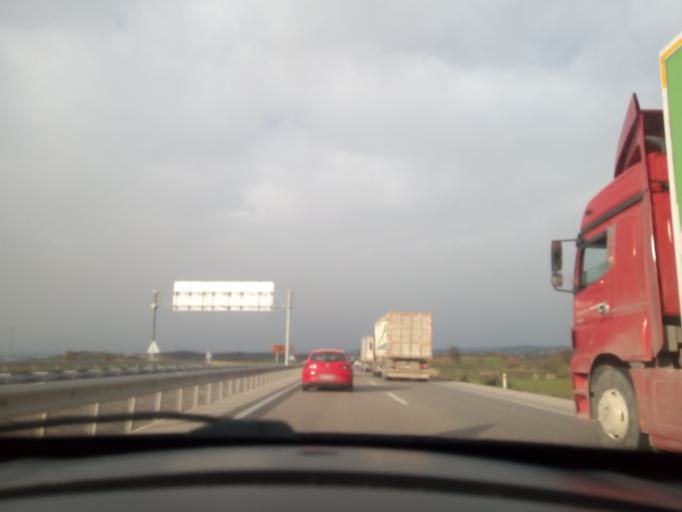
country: TR
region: Bursa
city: Mahmudiye
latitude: 40.2130
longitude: 28.6801
